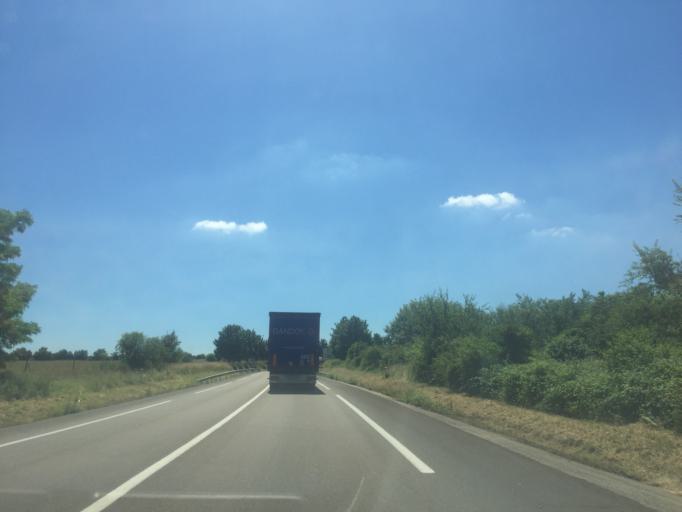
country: FR
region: Rhone-Alpes
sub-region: Departement du Rhone
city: Pusignan
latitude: 45.7559
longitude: 5.0834
